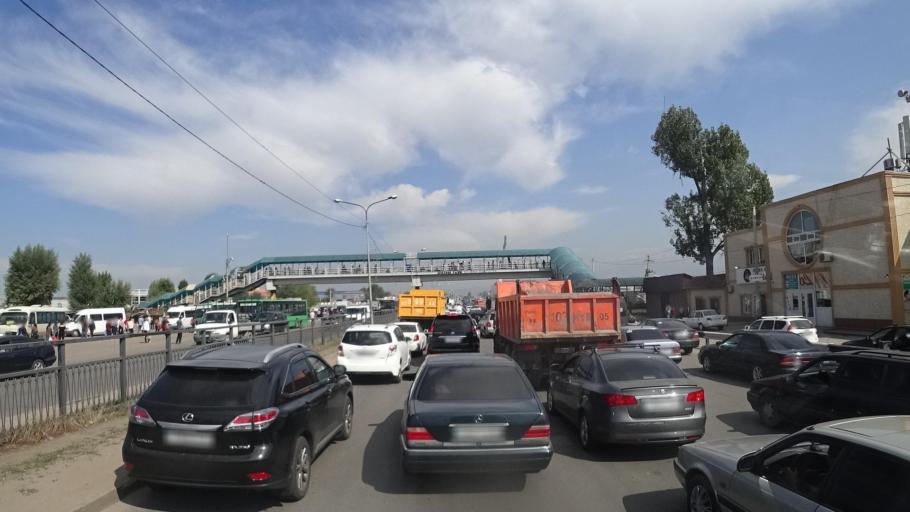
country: KZ
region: Almaty Oblysy
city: Burunday
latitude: 43.2305
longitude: 76.7716
